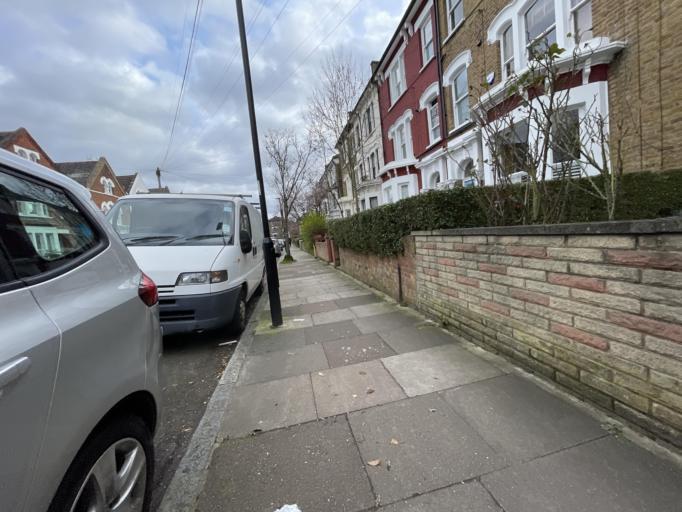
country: GB
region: England
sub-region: Greater London
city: Holloway
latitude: 51.5595
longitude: -0.1269
